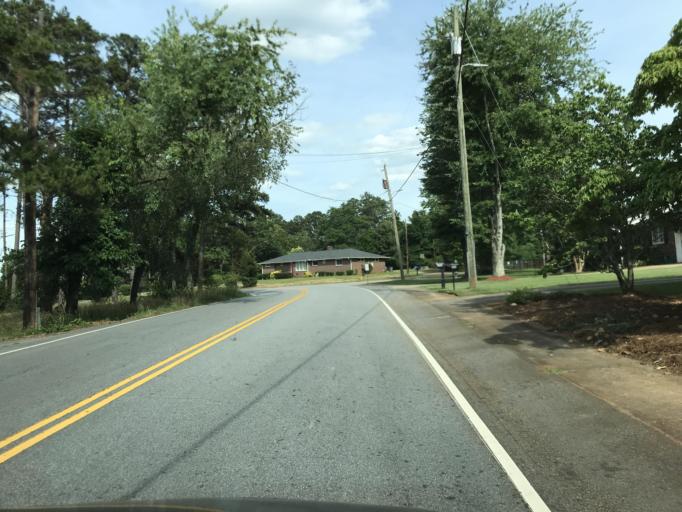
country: US
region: South Carolina
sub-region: Greenville County
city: Gantt
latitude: 34.7993
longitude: -82.3999
